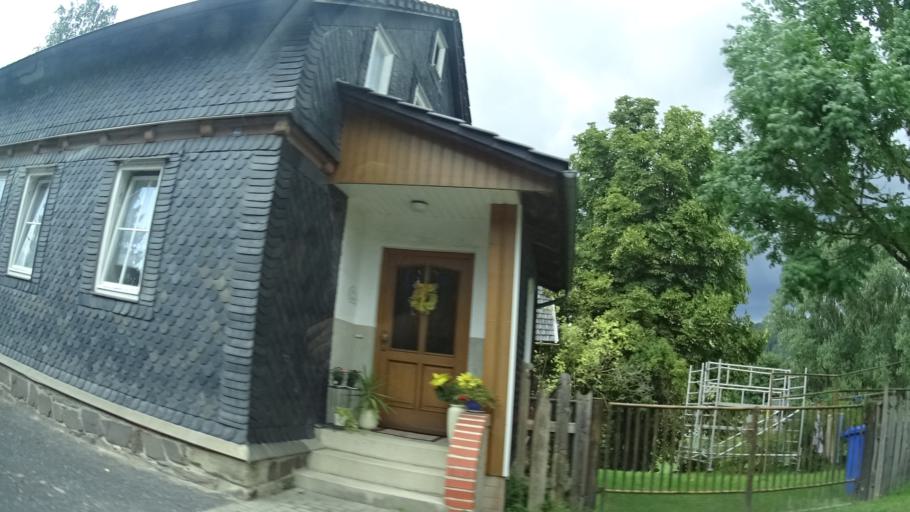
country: DE
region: Bavaria
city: Foritz
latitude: 50.3487
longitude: 11.2067
